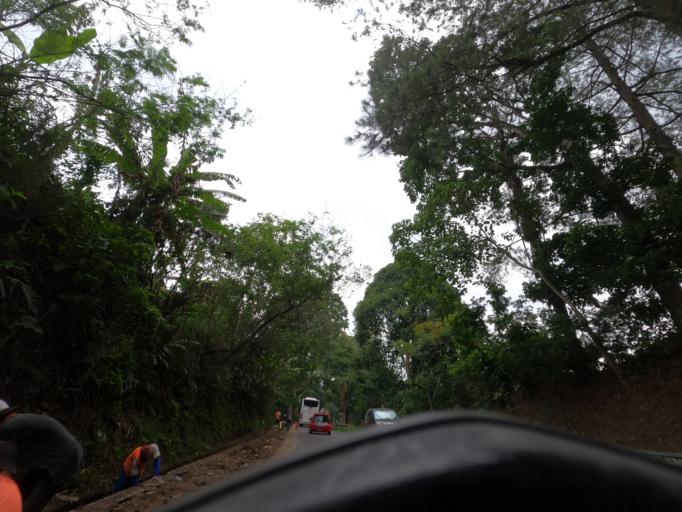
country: ID
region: West Java
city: Ciranjang-hilir
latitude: -6.7926
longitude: 107.0747
